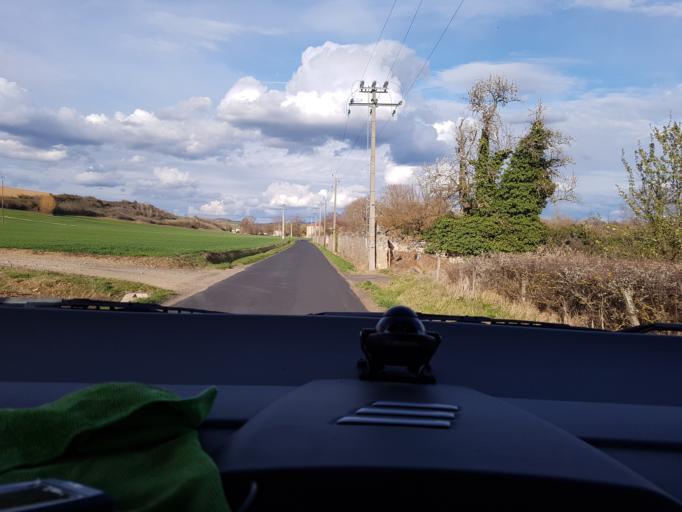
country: FR
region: Auvergne
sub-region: Departement du Puy-de-Dome
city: Saint-Germain-Lembron
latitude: 45.4559
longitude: 3.2164
